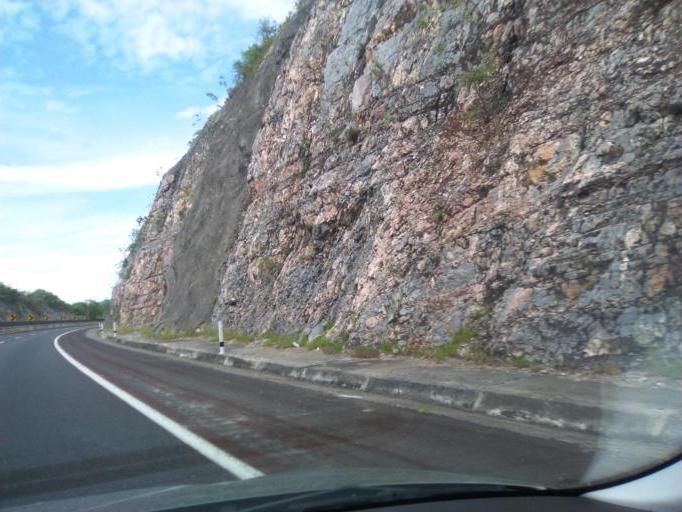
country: MX
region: Guerrero
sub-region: Eduardo Neri
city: Axaxacualco
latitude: 17.7890
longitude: -99.4856
